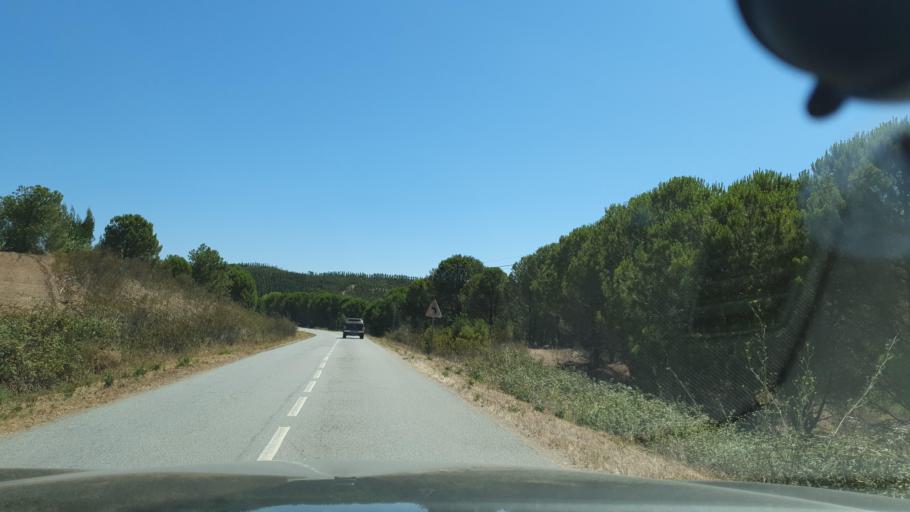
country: PT
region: Faro
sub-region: Monchique
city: Monchique
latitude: 37.4249
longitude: -8.5355
